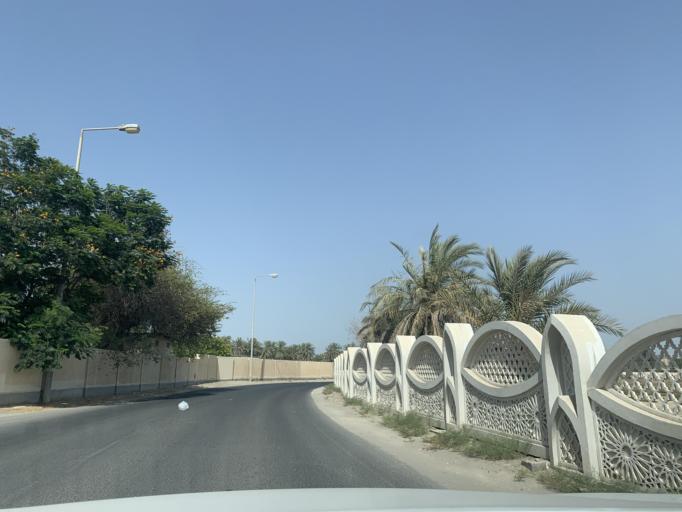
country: BH
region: Manama
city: Jidd Hafs
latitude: 26.2268
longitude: 50.4633
